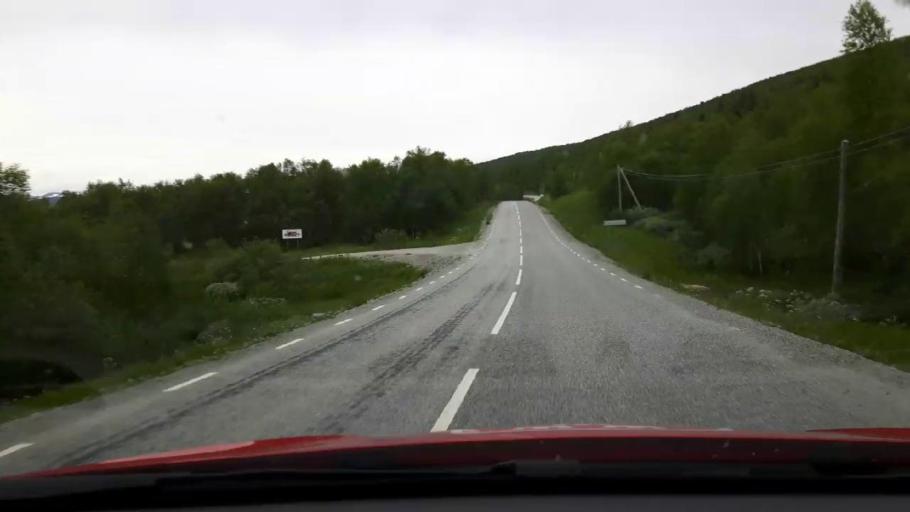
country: NO
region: Sor-Trondelag
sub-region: Tydal
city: Aas
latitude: 62.6635
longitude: 12.4293
